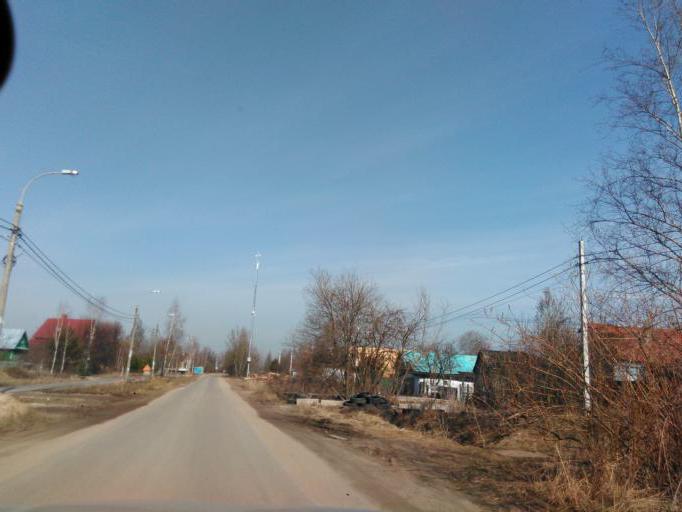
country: RU
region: Moskovskaya
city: Opalikha
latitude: 55.8767
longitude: 37.2689
